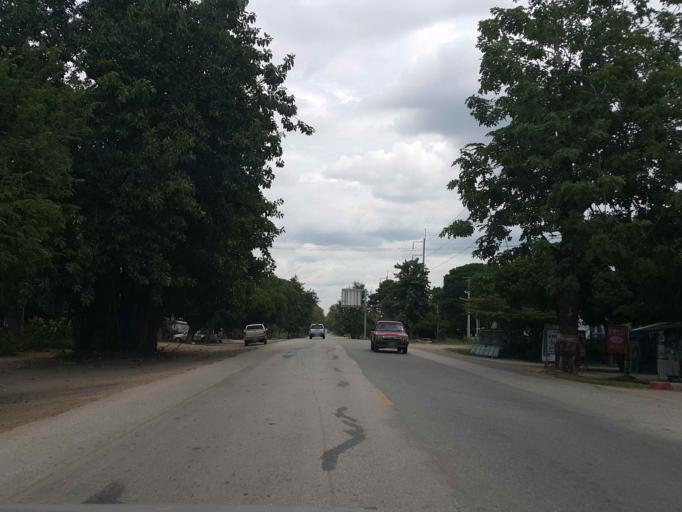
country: TH
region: Chiang Mai
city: Doi Lo
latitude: 18.4277
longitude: 98.8642
